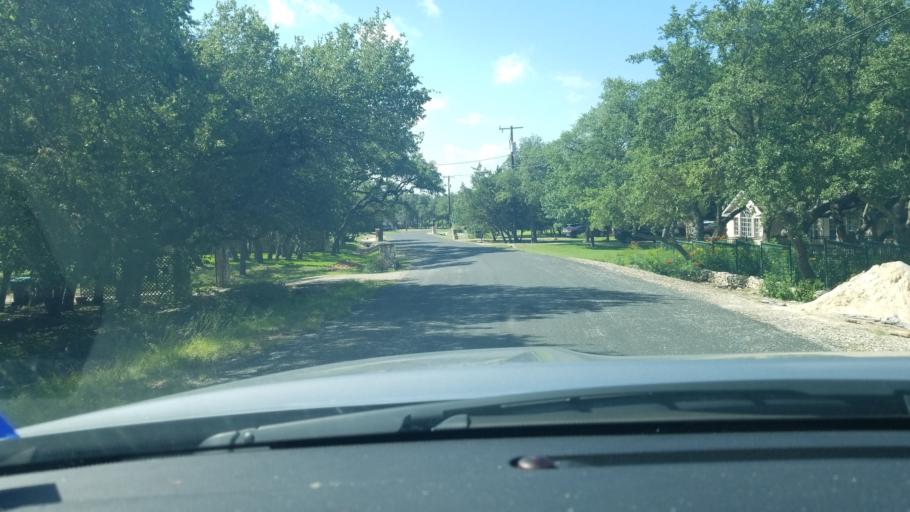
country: US
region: Texas
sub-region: Bexar County
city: Timberwood Park
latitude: 29.6914
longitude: -98.4889
